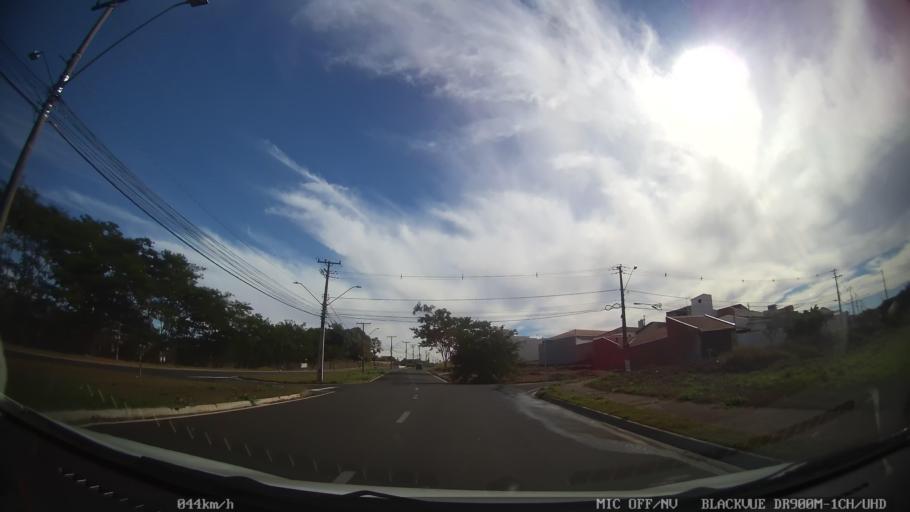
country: BR
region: Sao Paulo
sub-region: Catanduva
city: Catanduva
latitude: -21.1229
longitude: -48.9774
